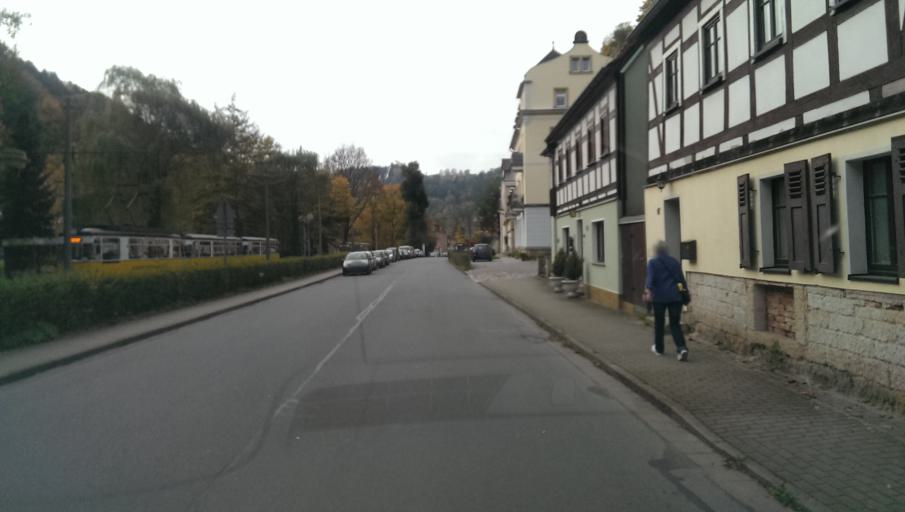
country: DE
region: Saxony
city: Bad Schandau
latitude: 50.9216
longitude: 14.1582
